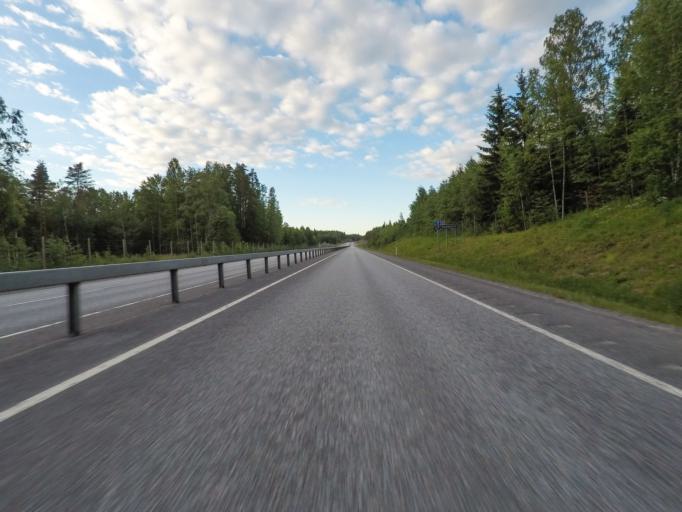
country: FI
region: Southern Savonia
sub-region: Mikkeli
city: Maentyharju
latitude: 61.4593
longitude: 26.7157
